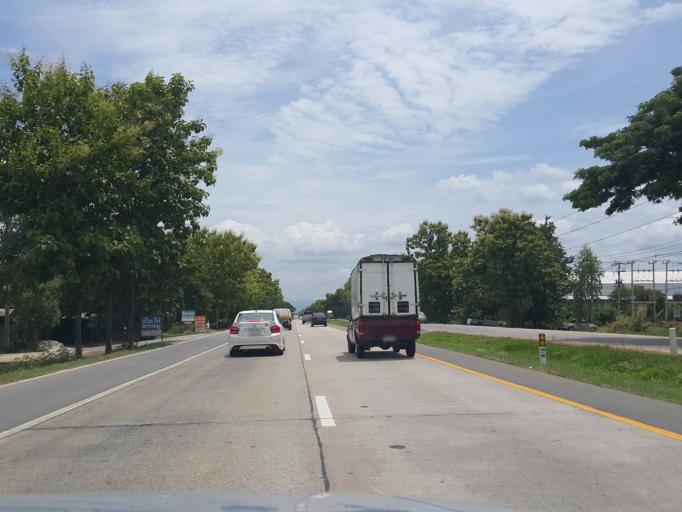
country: TH
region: Chiang Mai
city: Saraphi
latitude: 18.6661
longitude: 99.0519
